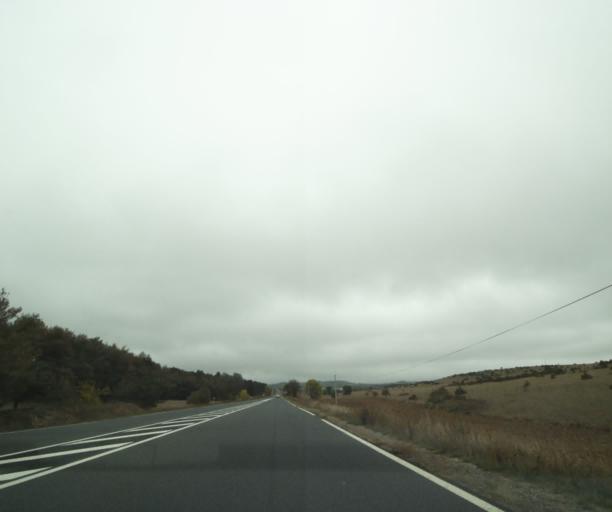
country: FR
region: Midi-Pyrenees
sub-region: Departement de l'Aveyron
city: La Cavalerie
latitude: 44.0322
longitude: 3.1473
